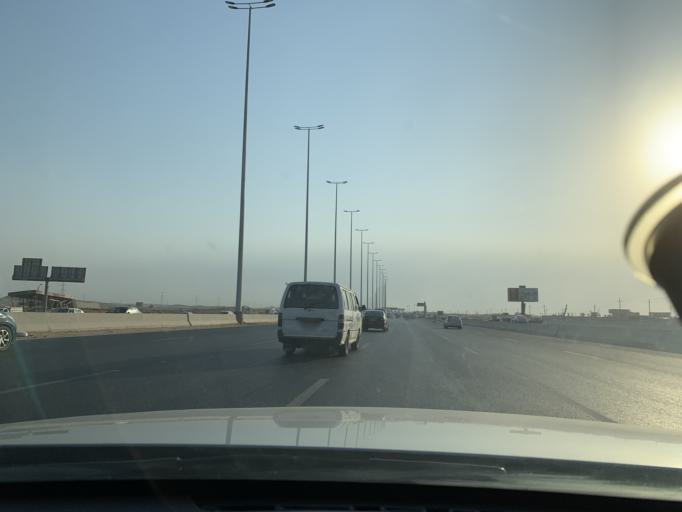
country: EG
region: Muhafazat al Qalyubiyah
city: Al Khankah
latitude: 30.1023
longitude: 31.5834
